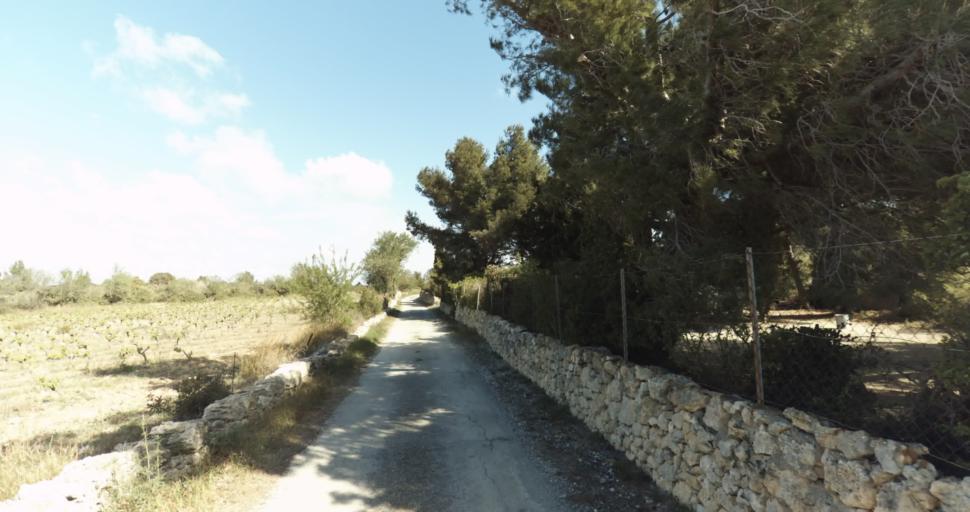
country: FR
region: Languedoc-Roussillon
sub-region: Departement de l'Aude
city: Leucate
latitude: 42.9273
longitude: 3.0310
